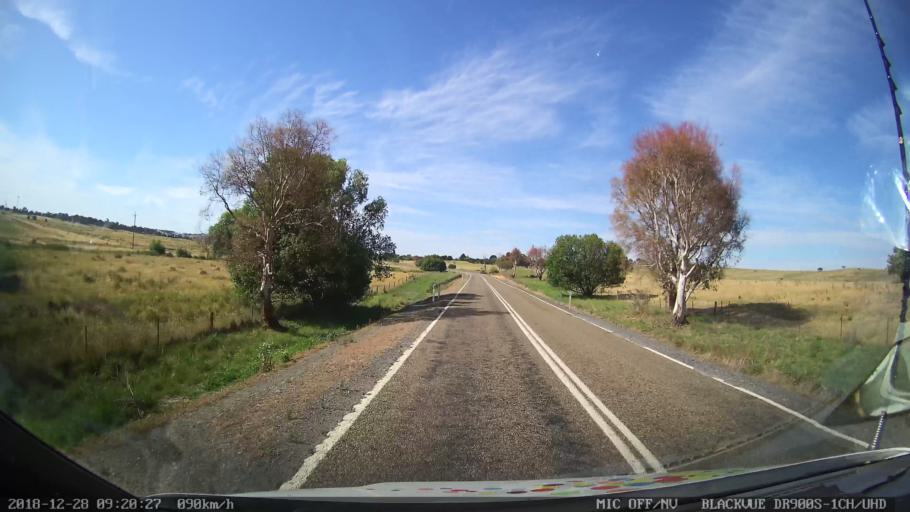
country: AU
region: New South Wales
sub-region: Upper Lachlan Shire
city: Crookwell
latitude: -34.3498
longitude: 149.3723
